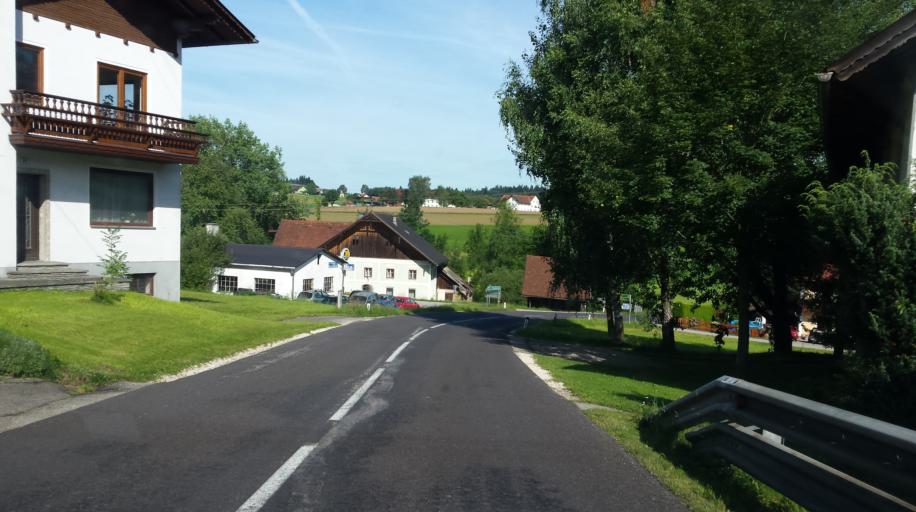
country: AT
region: Upper Austria
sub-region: Politischer Bezirk Vocklabruck
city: Frankenmarkt
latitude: 47.9705
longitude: 13.4176
